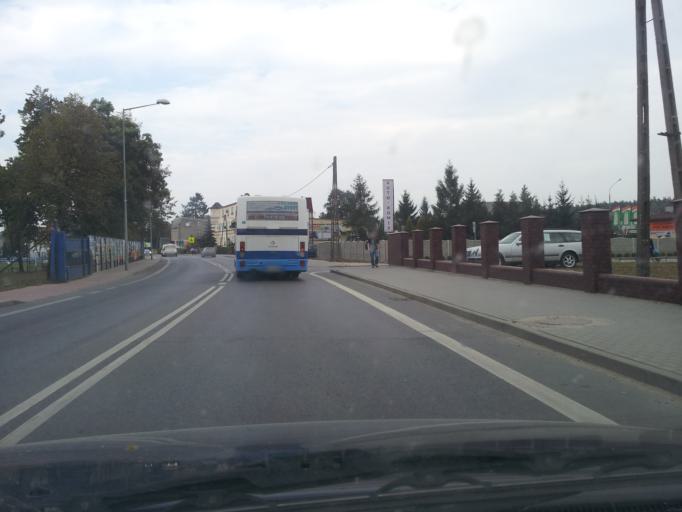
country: PL
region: Warmian-Masurian Voivodeship
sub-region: Powiat nowomiejski
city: Nowe Miasto Lubawskie
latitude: 53.4179
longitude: 19.5943
